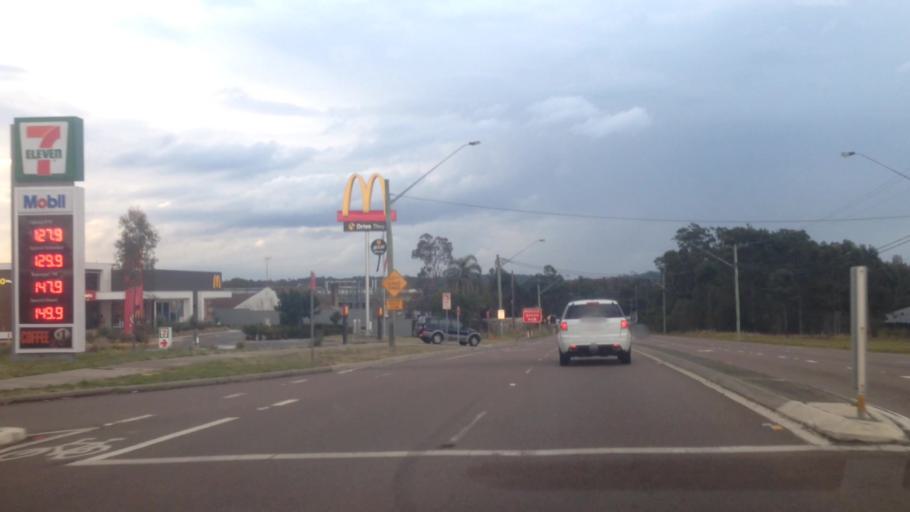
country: AU
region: New South Wales
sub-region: Wyong Shire
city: Tuggerawong
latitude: -33.2654
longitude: 151.4551
